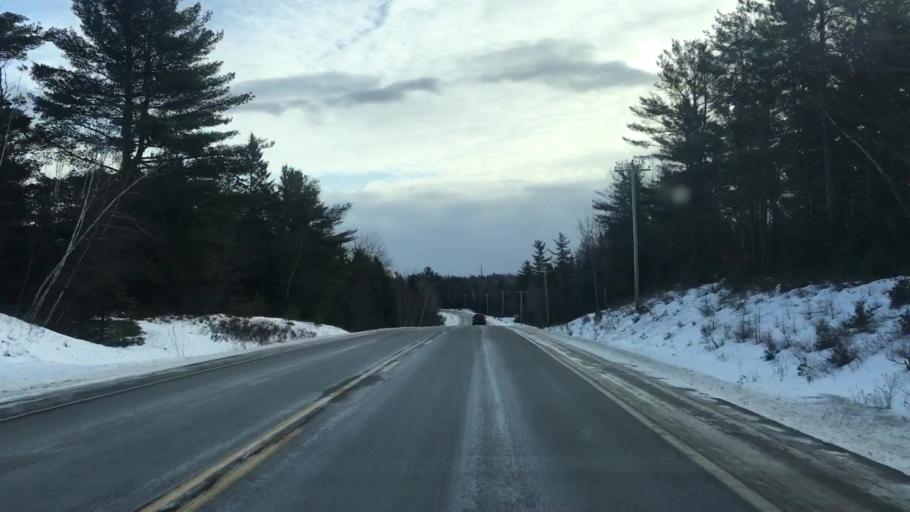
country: US
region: Maine
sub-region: Washington County
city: Machias
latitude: 45.0002
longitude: -67.6105
